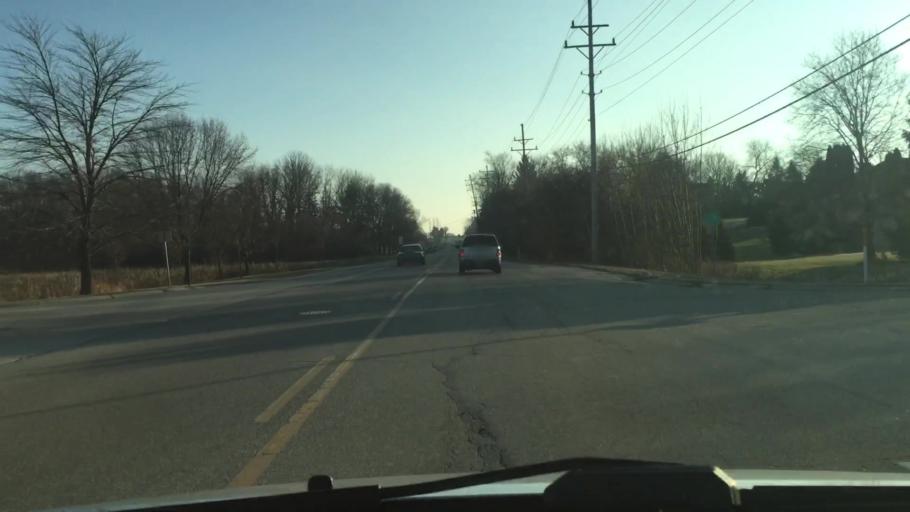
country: US
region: Wisconsin
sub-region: Waukesha County
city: Oconomowoc
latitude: 43.0964
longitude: -88.4958
